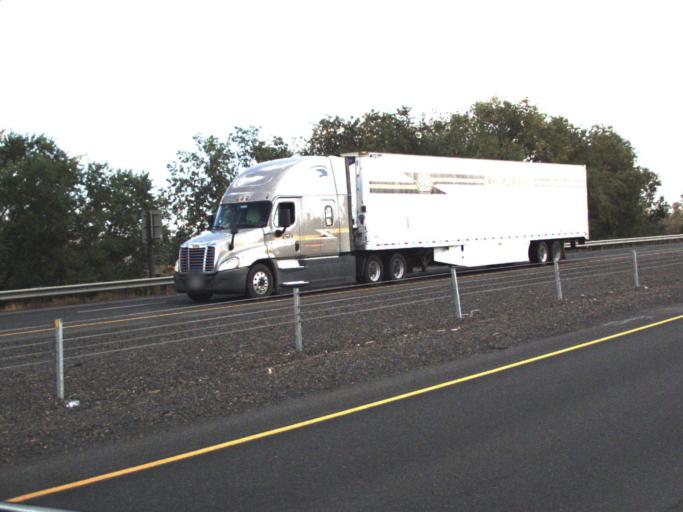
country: US
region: Washington
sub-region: Yakima County
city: Yakima
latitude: 46.5987
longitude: -120.4807
